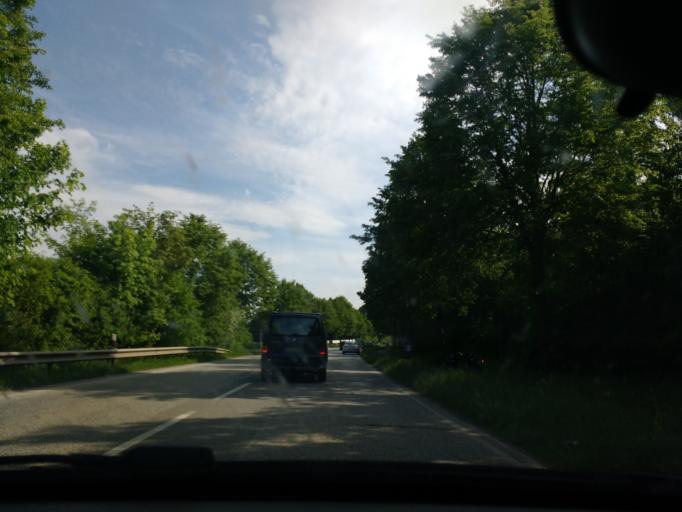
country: DE
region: Schleswig-Holstein
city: Buchholz
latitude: 53.7300
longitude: 10.7382
